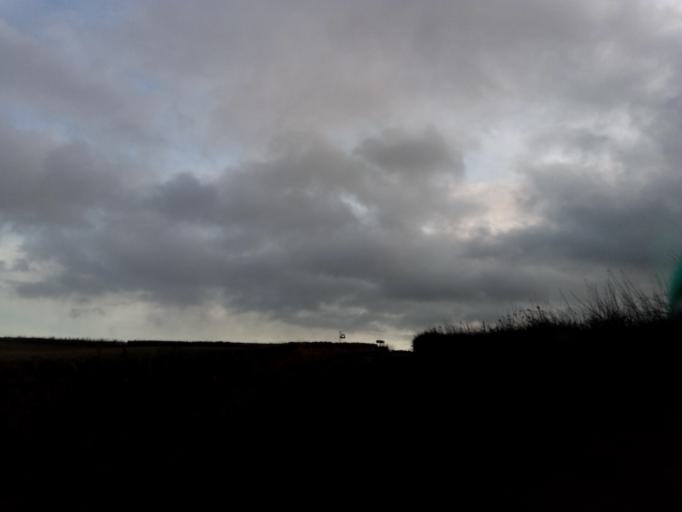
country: GB
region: Scotland
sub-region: The Scottish Borders
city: Selkirk
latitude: 55.5575
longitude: -2.7847
